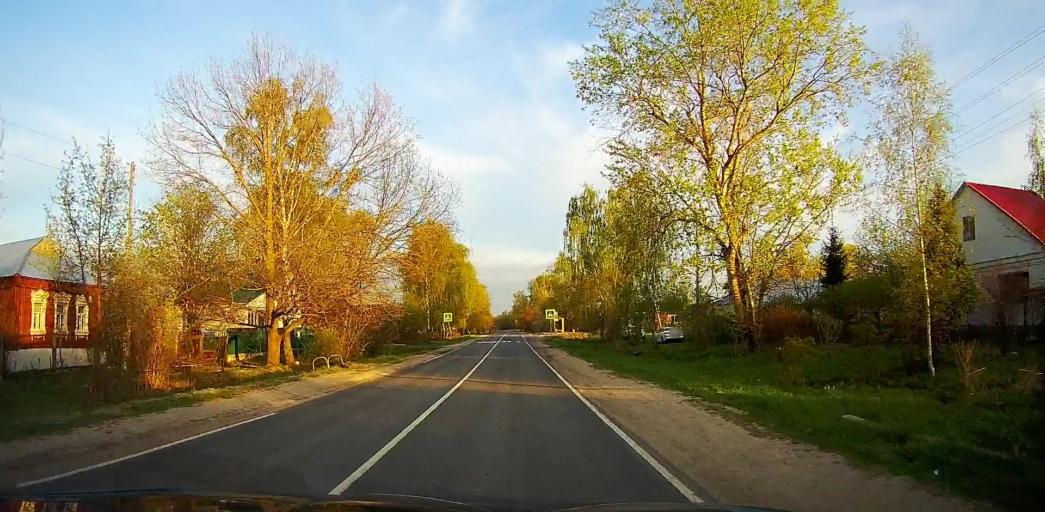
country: RU
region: Moskovskaya
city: Peski
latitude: 55.2129
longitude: 38.6733
